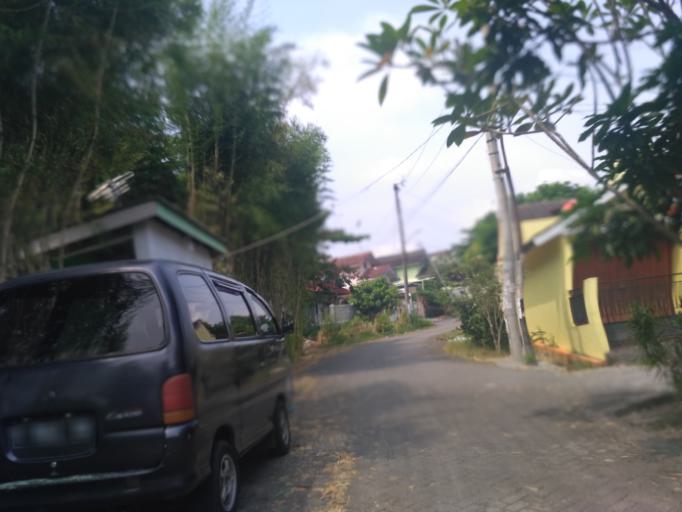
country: ID
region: Central Java
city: Mranggen
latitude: -7.0637
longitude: 110.4592
